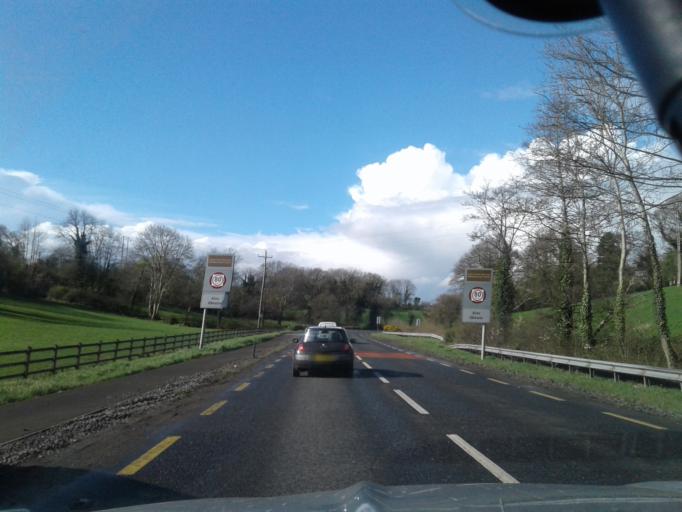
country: IE
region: Ulster
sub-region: County Monaghan
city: Monaghan
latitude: 54.2655
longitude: -6.9602
